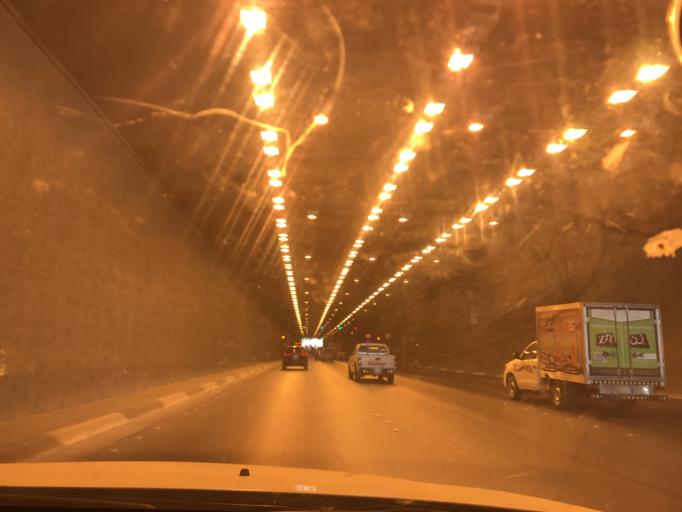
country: SA
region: Ar Riyad
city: Riyadh
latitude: 24.7315
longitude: 46.7266
